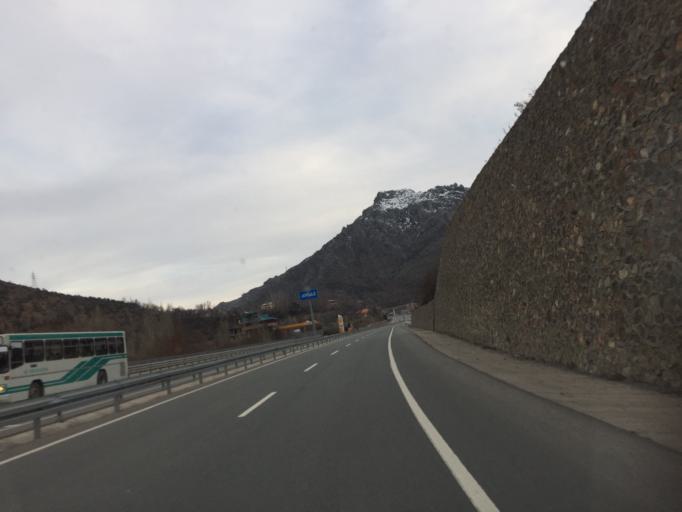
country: TR
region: Gumushane
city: Torul
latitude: 40.5455
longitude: 39.3235
